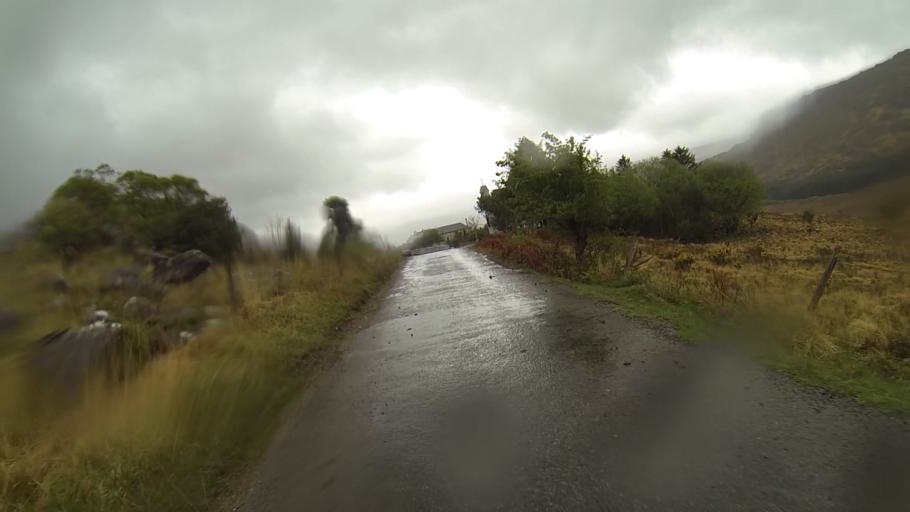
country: IE
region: Munster
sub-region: Ciarrai
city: Kenmare
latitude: 51.9868
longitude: -9.6536
